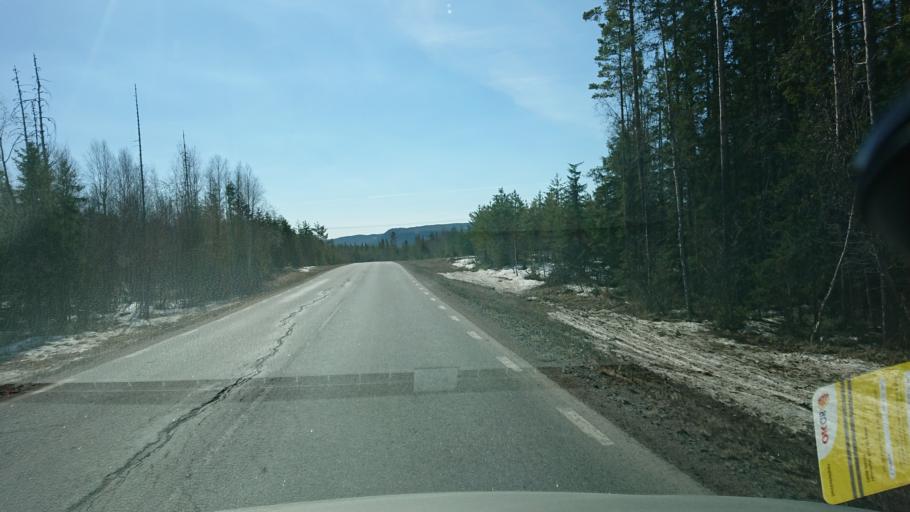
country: SE
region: Vaesternorrland
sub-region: Solleftea Kommun
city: As
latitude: 63.5831
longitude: 16.4360
